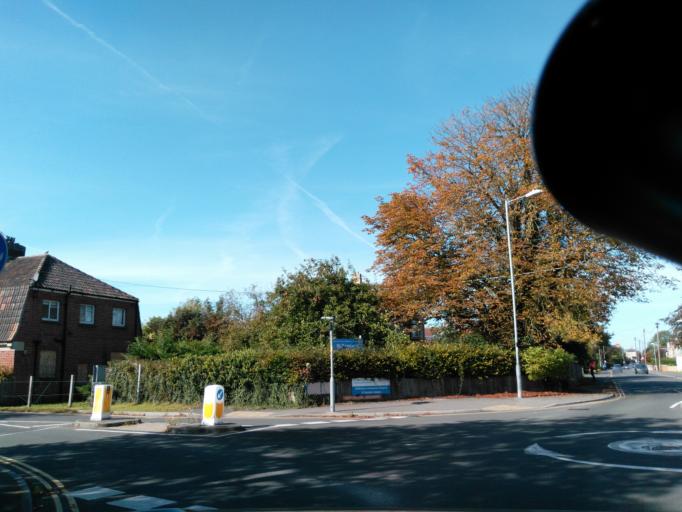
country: GB
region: England
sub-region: Wiltshire
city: Melksham
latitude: 51.3682
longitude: -2.1308
